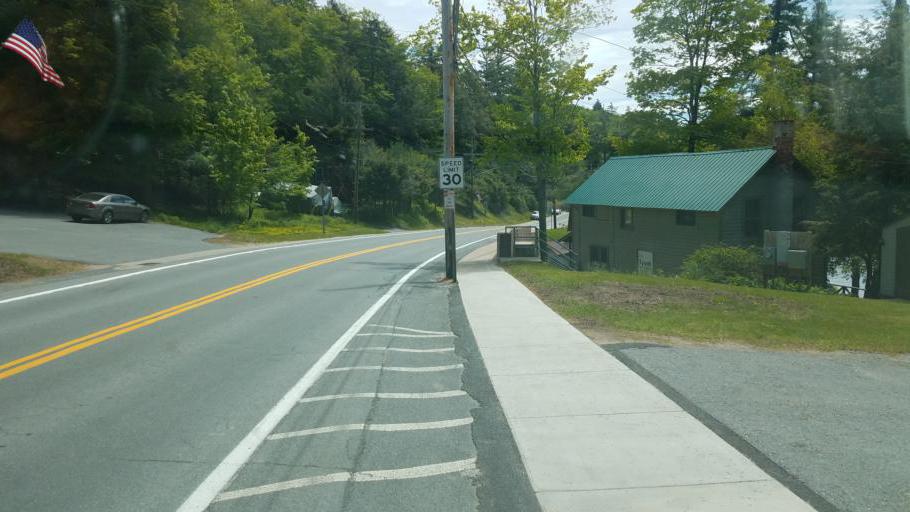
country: US
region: New York
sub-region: Hamilton County
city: Lake Pleasant
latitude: 43.7501
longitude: -74.7929
